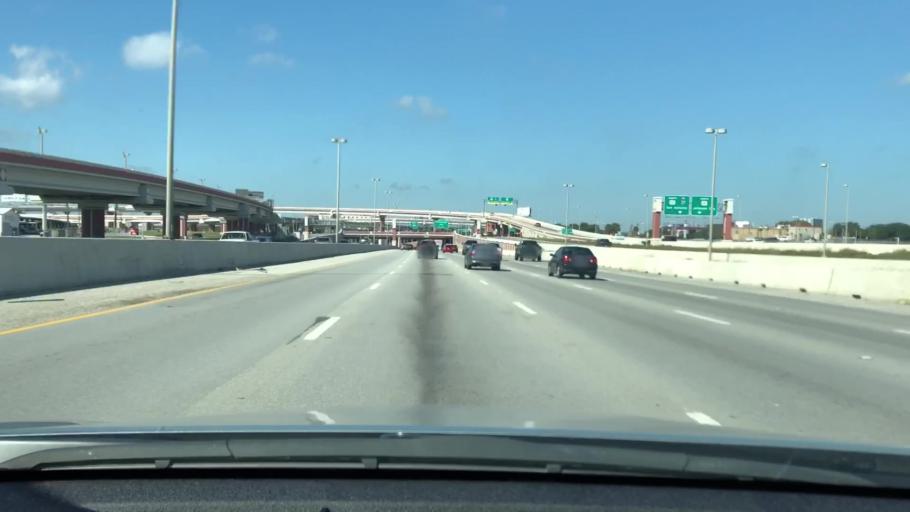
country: US
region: Texas
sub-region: Bexar County
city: Alamo Heights
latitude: 29.5192
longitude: -98.4734
